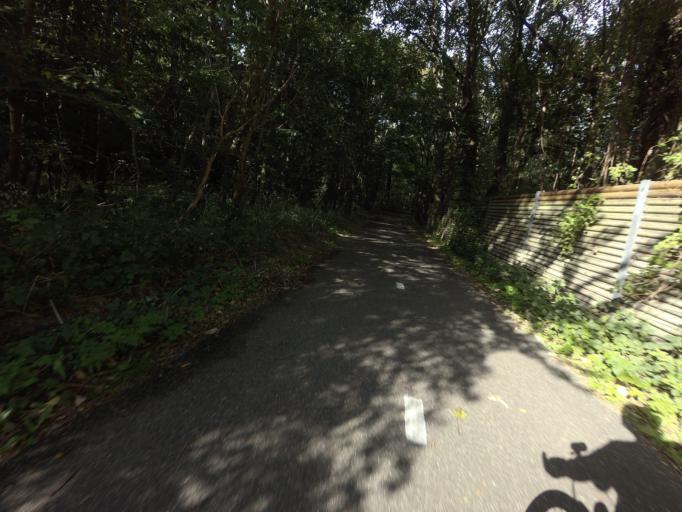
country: NL
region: Zeeland
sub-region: Gemeente Vlissingen
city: Vlissingen
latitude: 51.4907
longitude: 3.5052
